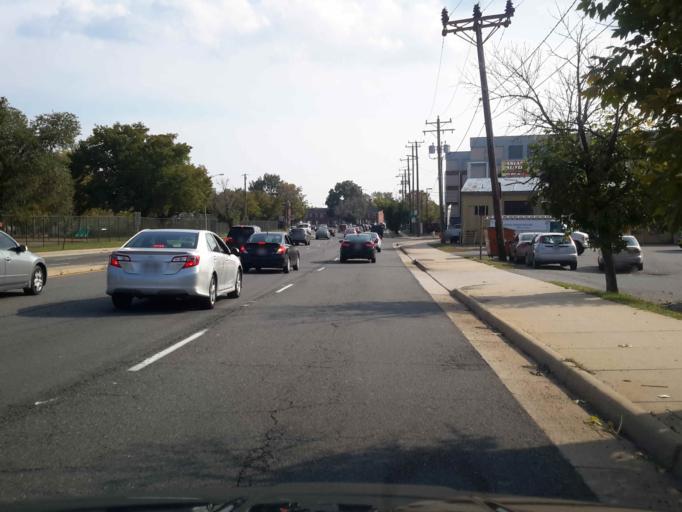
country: US
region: Virginia
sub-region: City of Alexandria
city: Alexandria
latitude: 38.8184
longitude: -77.0495
